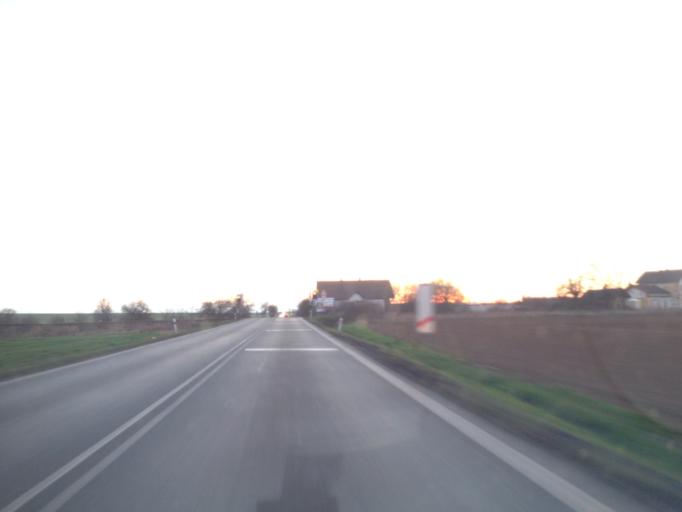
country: CZ
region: Central Bohemia
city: Rakovnik
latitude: 50.1675
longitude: 13.6440
